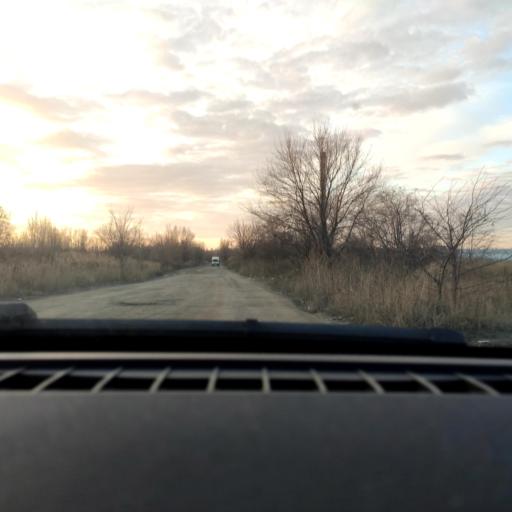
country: RU
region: Voronezj
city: Maslovka
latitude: 51.6138
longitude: 39.2676
